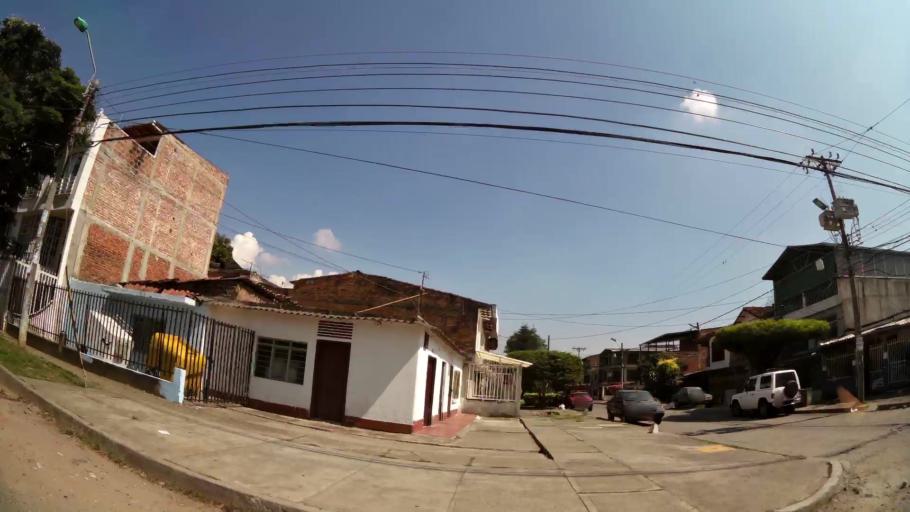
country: CO
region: Valle del Cauca
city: Cali
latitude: 3.4076
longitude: -76.5248
